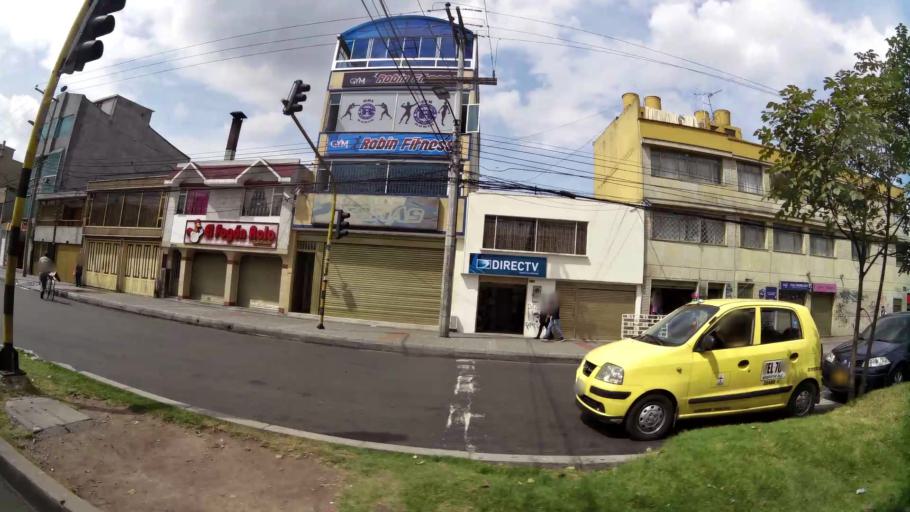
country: CO
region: Bogota D.C.
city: Bogota
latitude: 4.6026
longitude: -74.1115
